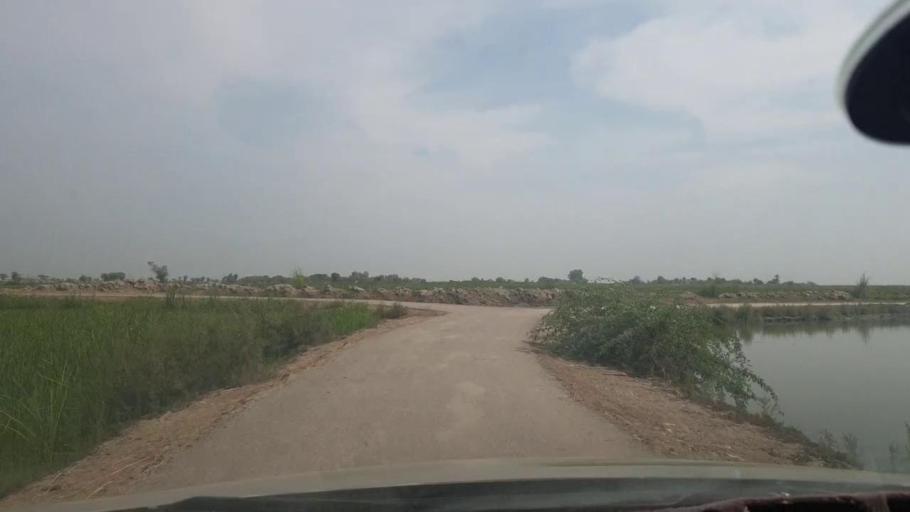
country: PK
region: Sindh
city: Jacobabad
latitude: 28.3103
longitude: 68.4772
